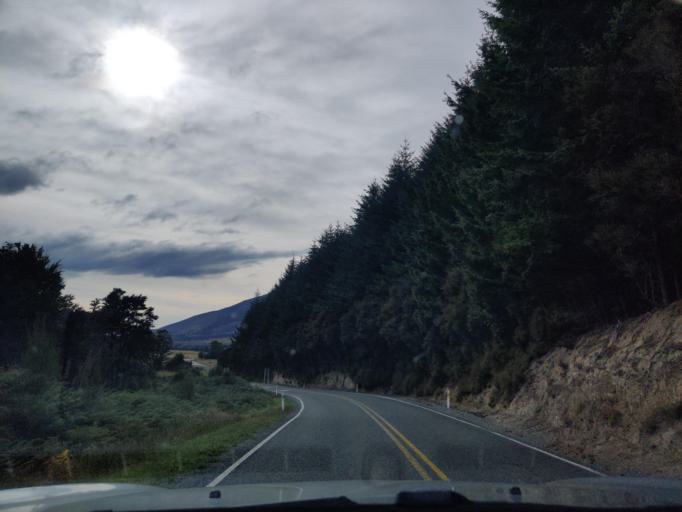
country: NZ
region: Tasman
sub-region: Tasman District
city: Wakefield
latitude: -41.7693
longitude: 172.9561
